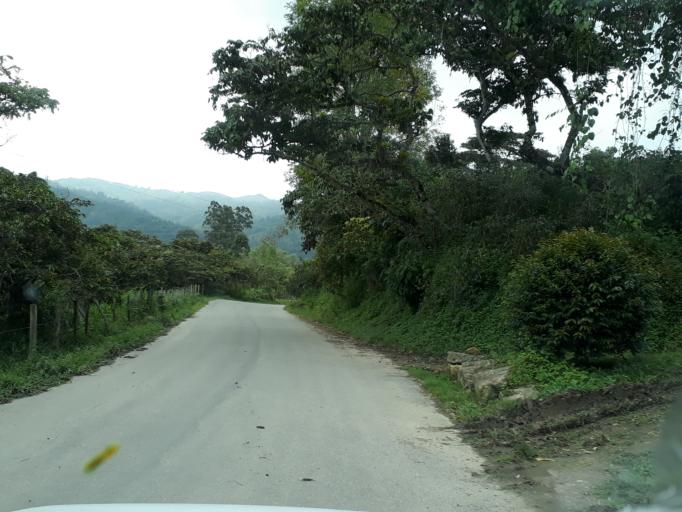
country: CO
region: Cundinamarca
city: Junin
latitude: 4.8143
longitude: -73.6713
